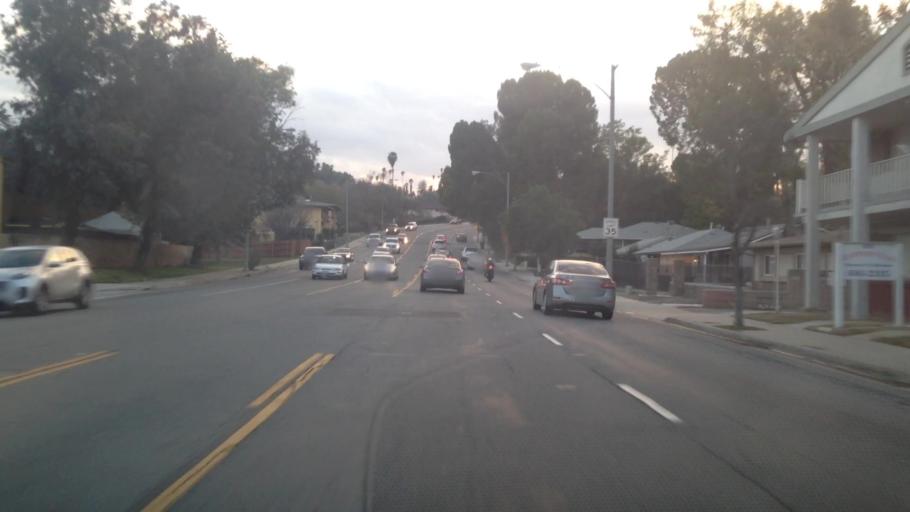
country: US
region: California
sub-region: Riverside County
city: Riverside
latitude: 33.9670
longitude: -117.3791
